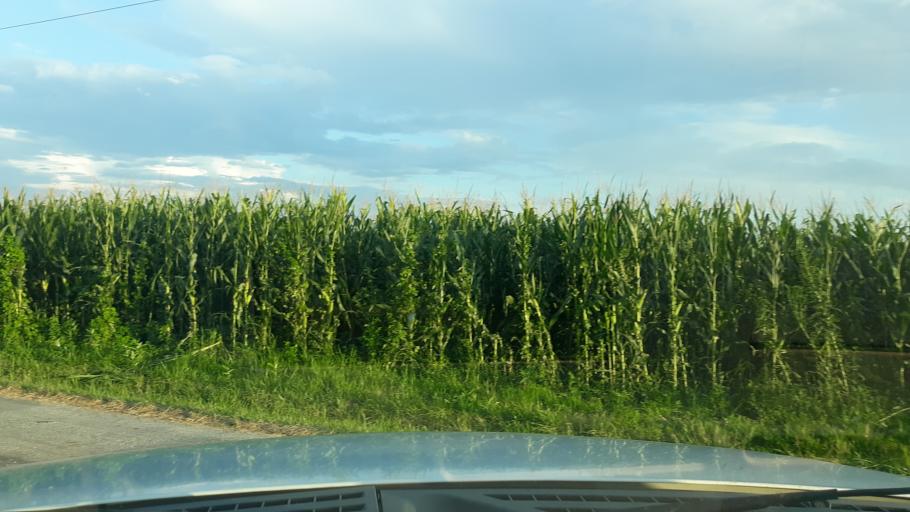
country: US
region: Illinois
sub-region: Saline County
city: Harrisburg
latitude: 37.8342
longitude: -88.6132
